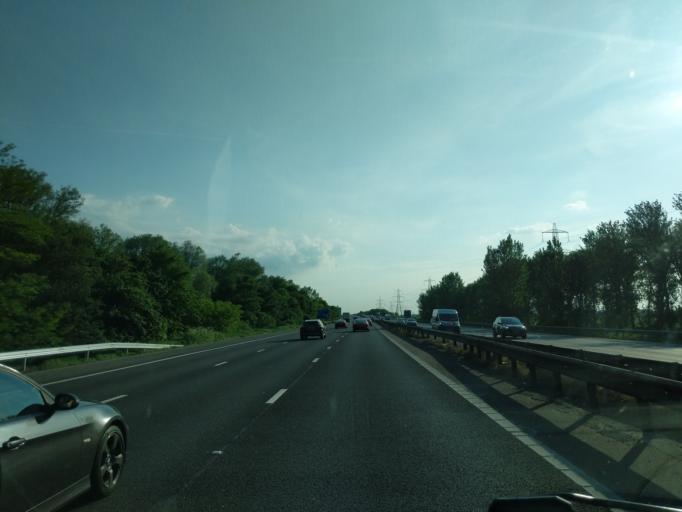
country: GB
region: England
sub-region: Cheshire West and Chester
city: Helsby
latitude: 53.2777
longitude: -2.7738
